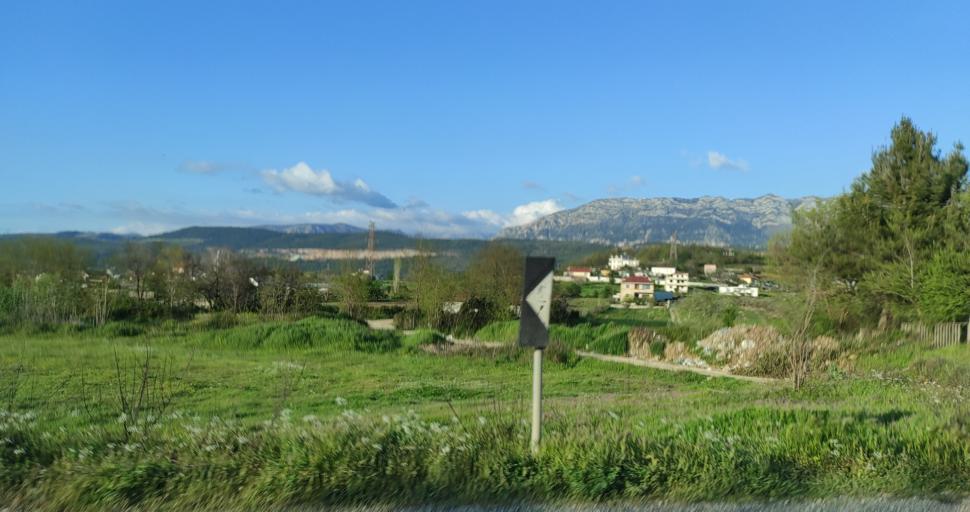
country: AL
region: Durres
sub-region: Rrethi i Krujes
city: Fushe-Kruje
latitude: 41.4838
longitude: 19.7332
